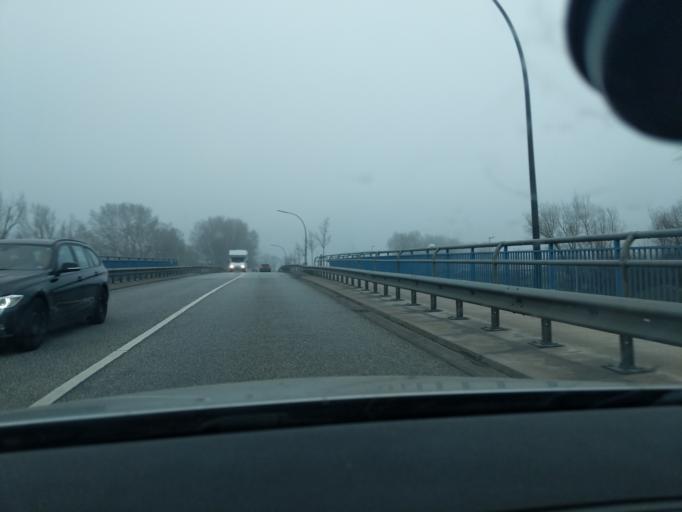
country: DE
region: Hamburg
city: Altona
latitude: 53.5168
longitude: 9.8806
